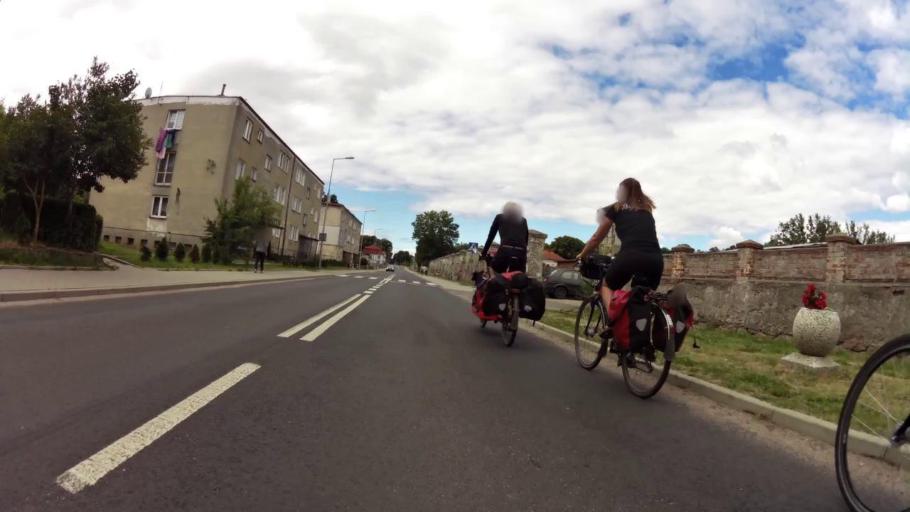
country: PL
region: West Pomeranian Voivodeship
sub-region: Powiat lobeski
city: Radowo Male
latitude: 53.7604
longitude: 15.5381
